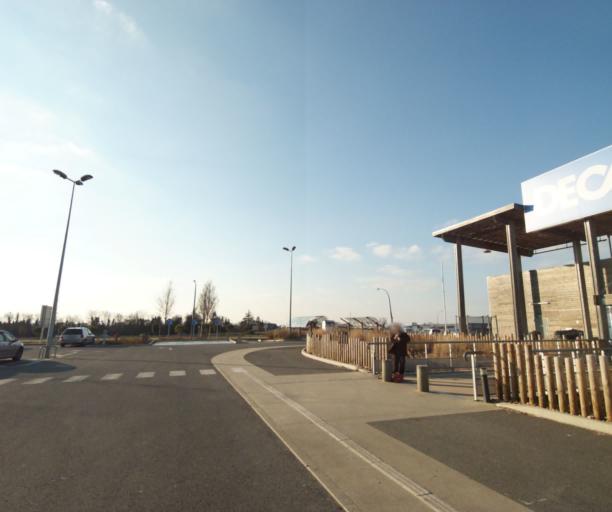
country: FR
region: Poitou-Charentes
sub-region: Departement des Deux-Sevres
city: Aiffres
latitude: 46.3162
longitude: -0.4186
